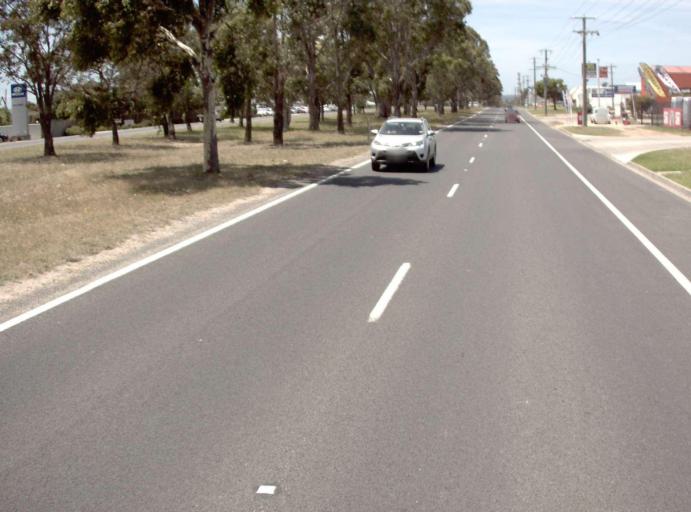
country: AU
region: Victoria
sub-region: East Gippsland
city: Bairnsdale
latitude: -37.8351
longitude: 147.6030
